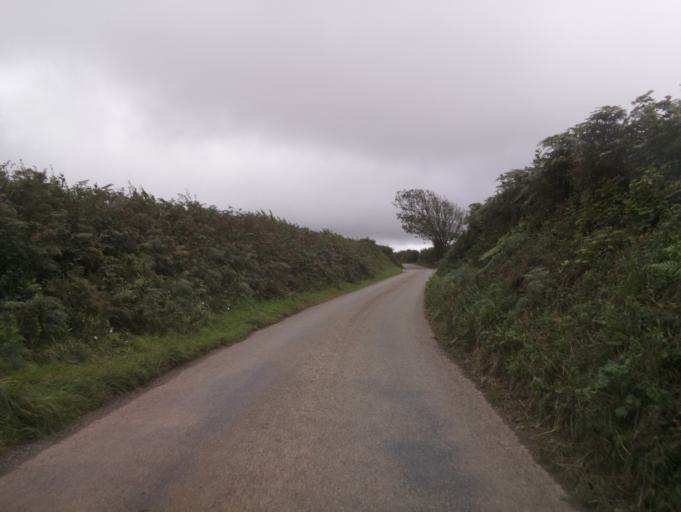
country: GB
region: England
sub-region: Devon
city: Kingsbridge
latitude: 50.3007
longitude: -3.7169
